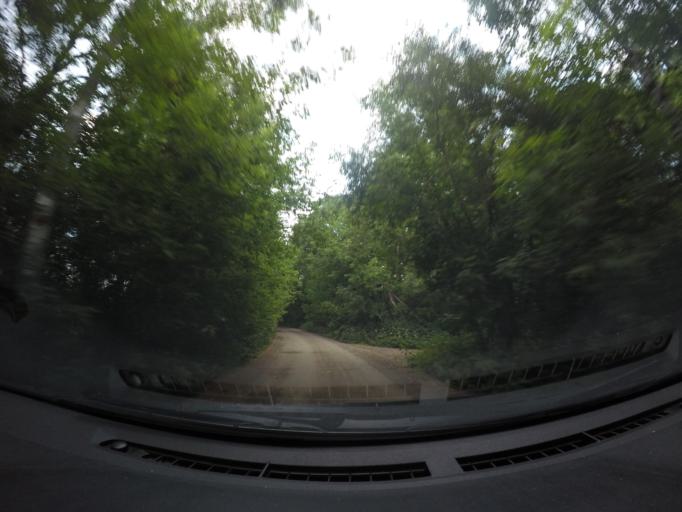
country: RU
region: Moskovskaya
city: Krasnyy Tkach
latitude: 55.4186
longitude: 39.2339
